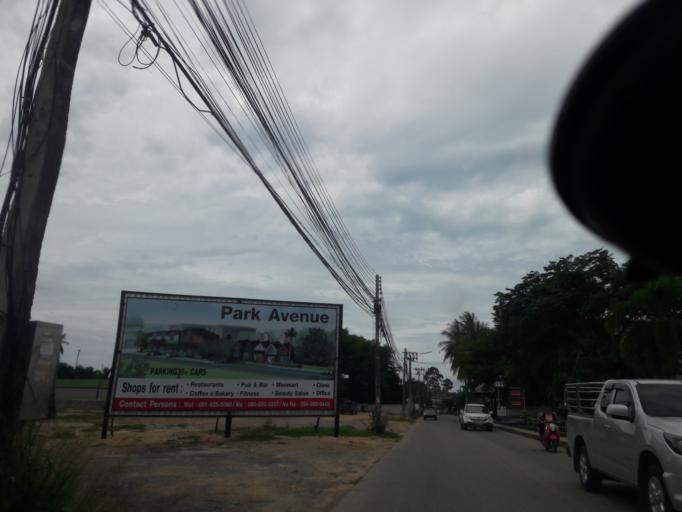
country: TH
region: Surat Thani
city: Ko Samui
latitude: 9.5356
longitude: 100.0427
